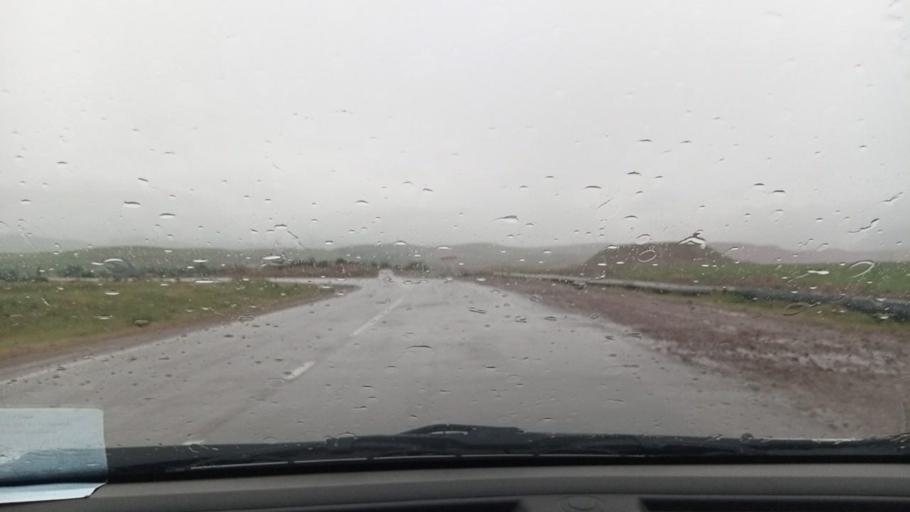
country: UZ
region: Toshkent
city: Angren
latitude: 41.0450
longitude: 70.1572
